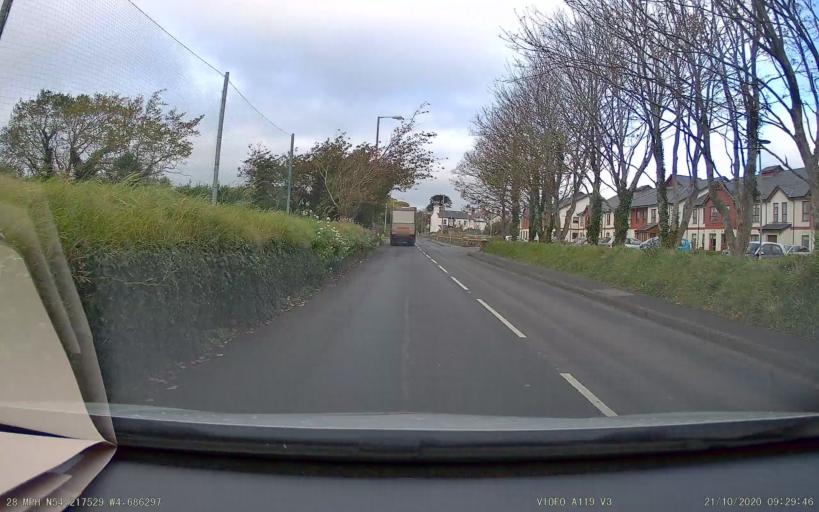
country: IM
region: Castletown
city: Castletown
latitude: 54.2175
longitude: -4.6862
